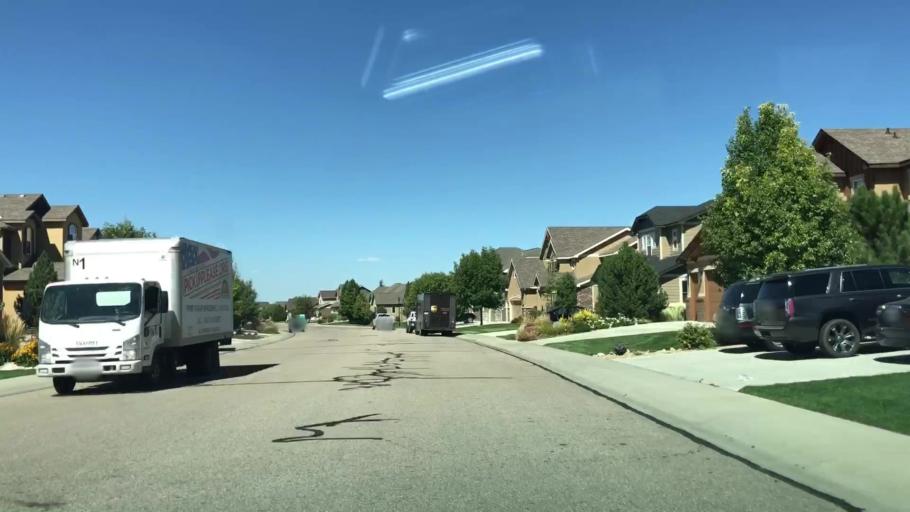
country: US
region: Colorado
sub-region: Weld County
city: Windsor
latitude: 40.4510
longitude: -104.9483
